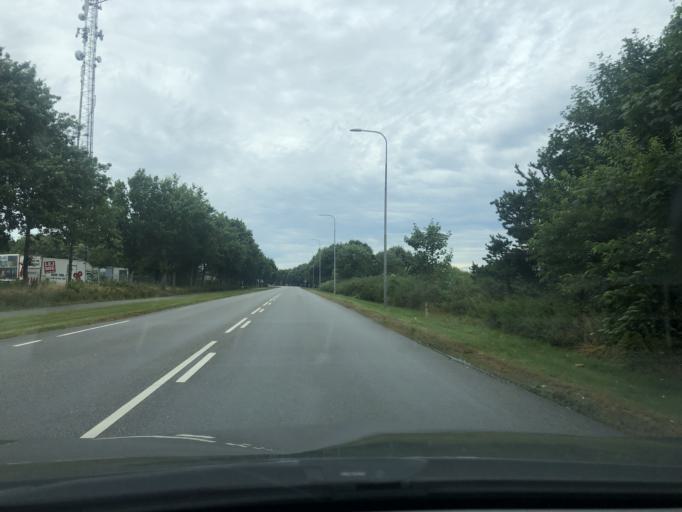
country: DK
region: South Denmark
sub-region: Billund Kommune
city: Grindsted
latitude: 55.7585
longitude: 8.9440
